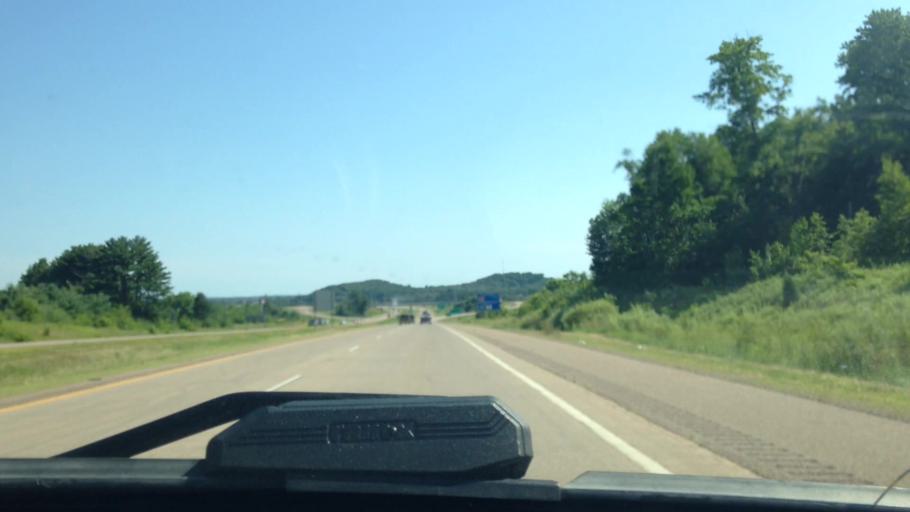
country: US
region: Wisconsin
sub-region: Chippewa County
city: Lake Hallie
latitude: 44.8542
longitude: -91.4335
